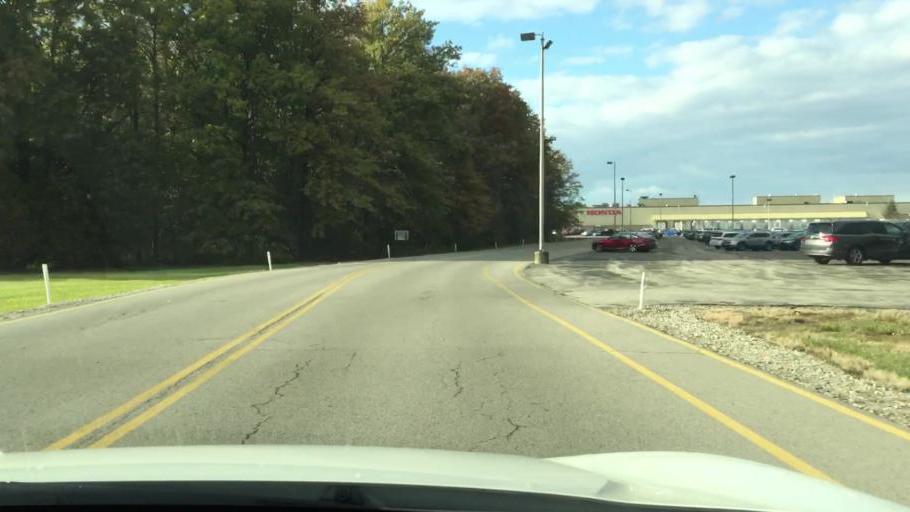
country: US
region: Ohio
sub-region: Champaign County
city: North Lewisburg
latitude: 40.2729
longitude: -83.4976
